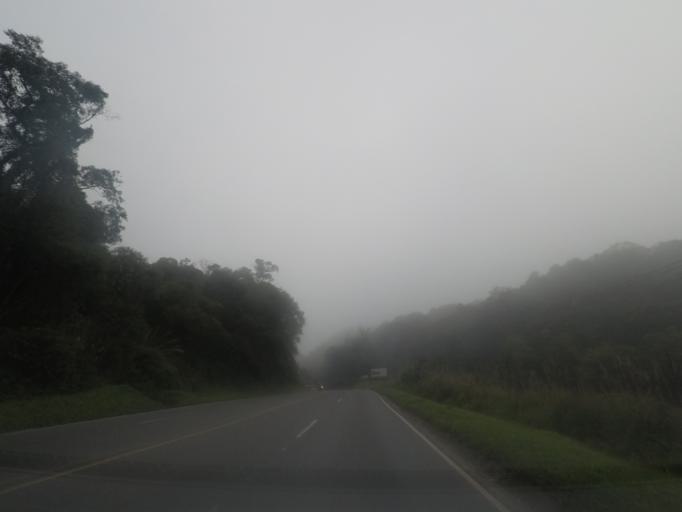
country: BR
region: Parana
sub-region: Almirante Tamandare
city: Almirante Tamandare
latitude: -25.2793
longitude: -49.3035
